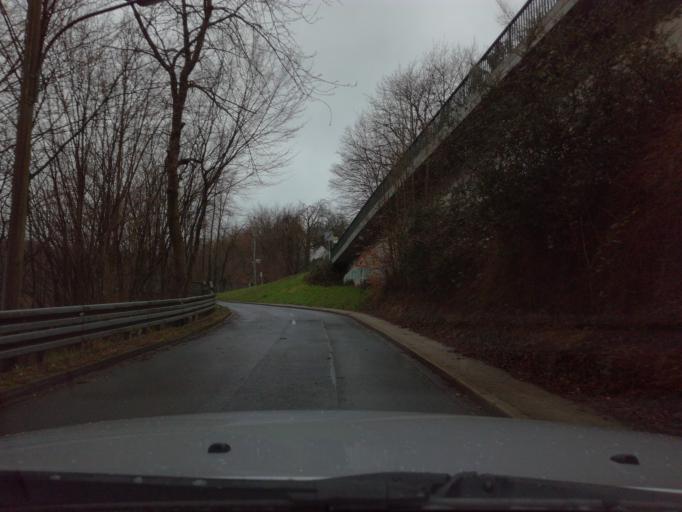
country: DE
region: North Rhine-Westphalia
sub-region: Regierungsbezirk Dusseldorf
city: Velbert
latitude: 51.3618
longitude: 7.1162
